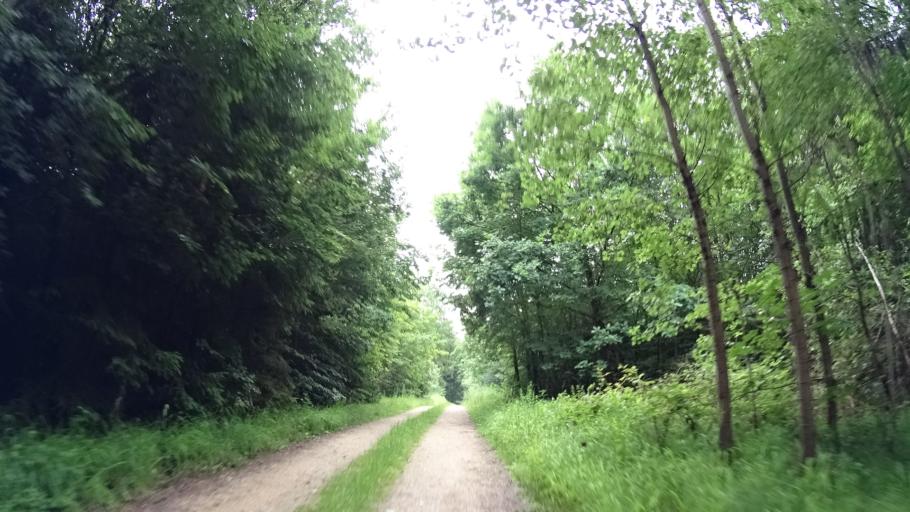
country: DE
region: Bavaria
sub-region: Upper Bavaria
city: Stammham
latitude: 48.8689
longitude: 11.4360
